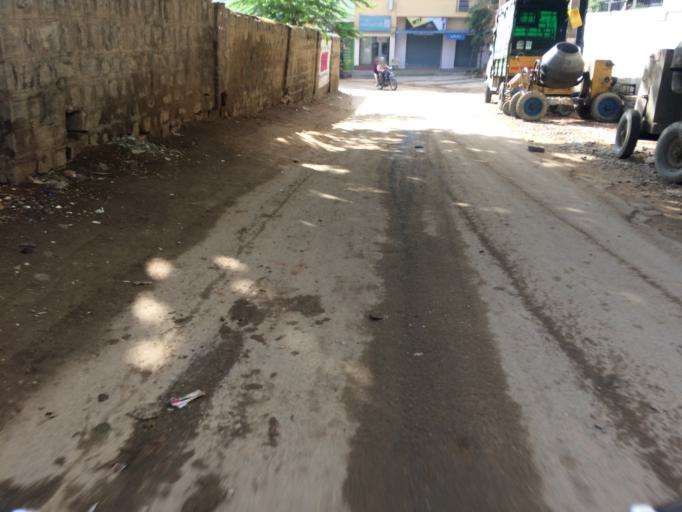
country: IN
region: Karnataka
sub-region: Bangalore Urban
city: Bangalore
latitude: 12.9127
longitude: 77.6233
